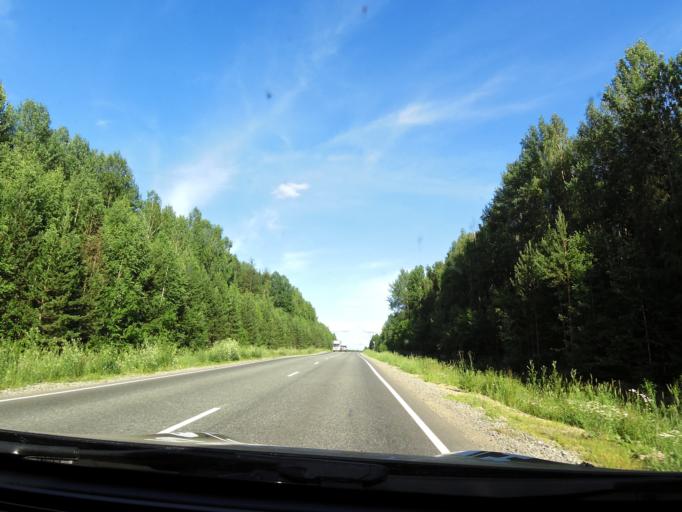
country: RU
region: Kirov
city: Chernaya Kholunitsa
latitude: 58.8615
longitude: 51.6075
